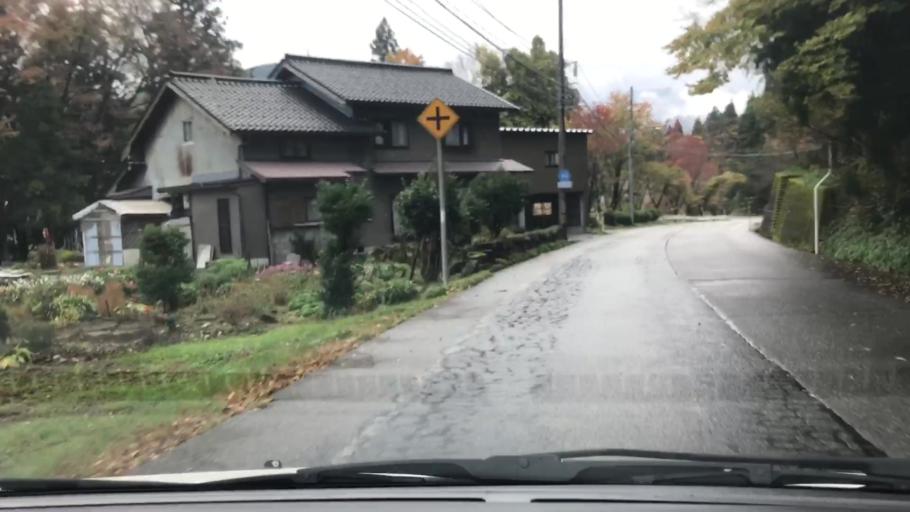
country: JP
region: Toyama
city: Kamiichi
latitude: 36.5824
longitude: 137.3271
